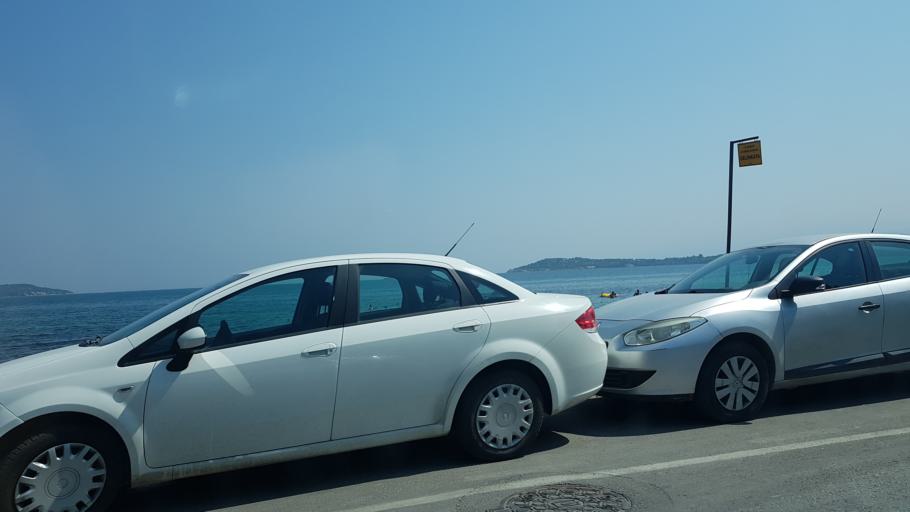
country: TR
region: Izmir
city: Urla
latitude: 38.3733
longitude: 26.7617
